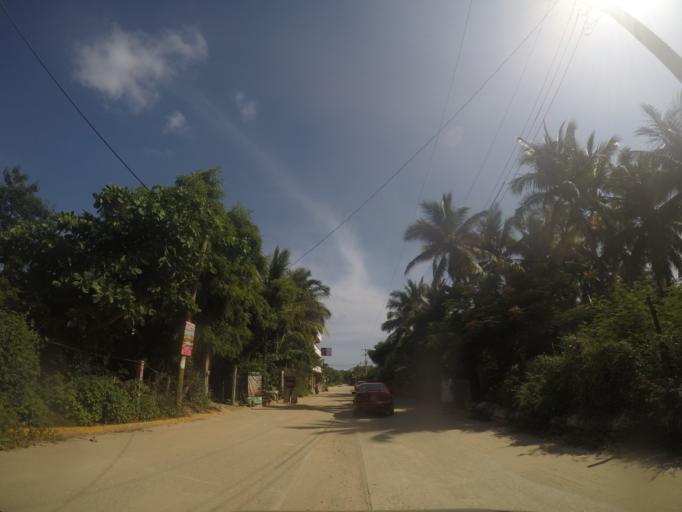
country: MX
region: Oaxaca
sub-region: Santa Maria Colotepec
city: Brisas de Zicatela
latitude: 15.8362
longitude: -97.0445
